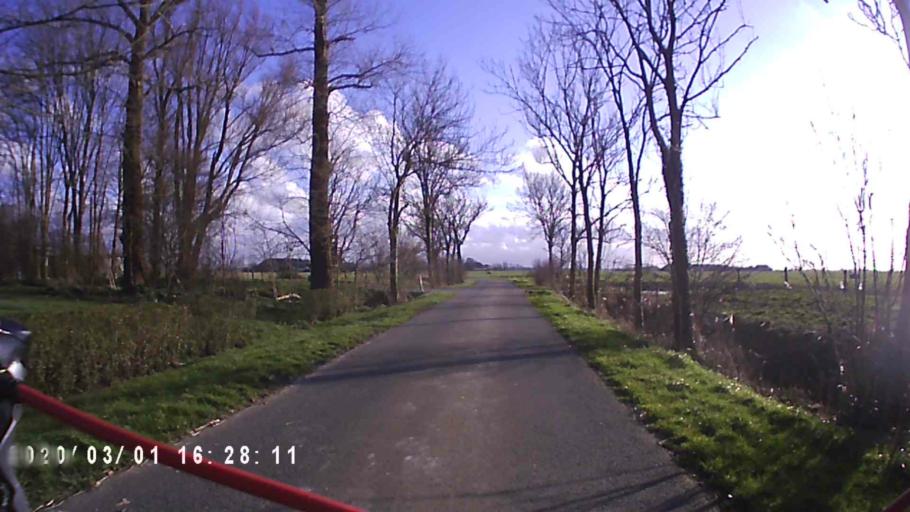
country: NL
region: Groningen
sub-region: Gemeente Zuidhorn
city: Oldehove
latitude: 53.3044
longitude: 6.4286
